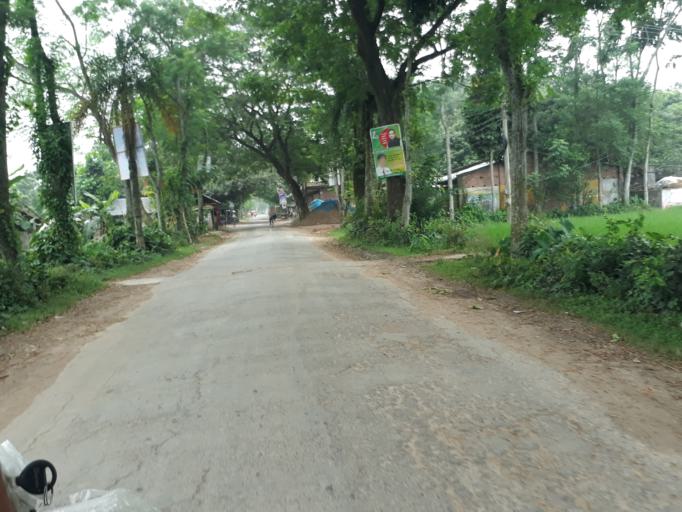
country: BD
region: Khulna
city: Kaliganj
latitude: 23.3514
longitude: 88.9237
